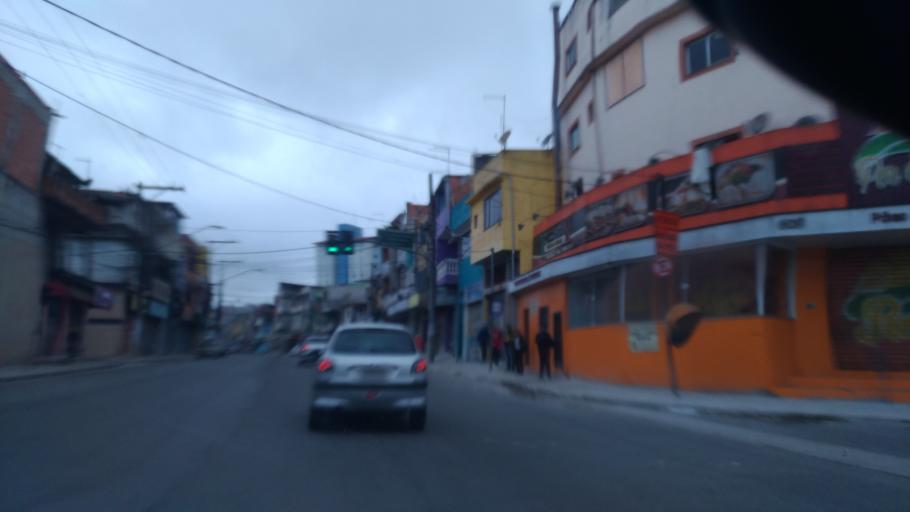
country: BR
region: Sao Paulo
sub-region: Sao Bernardo Do Campo
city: Sao Bernardo do Campo
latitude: -23.7096
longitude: -46.5287
